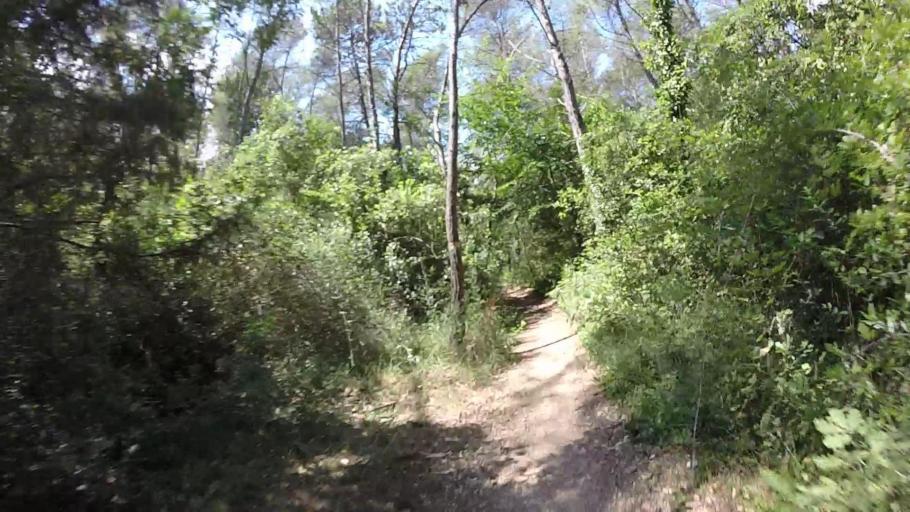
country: FR
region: Provence-Alpes-Cote d'Azur
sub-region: Departement des Alpes-Maritimes
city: Le Cannet
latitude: 43.5971
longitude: 7.0315
